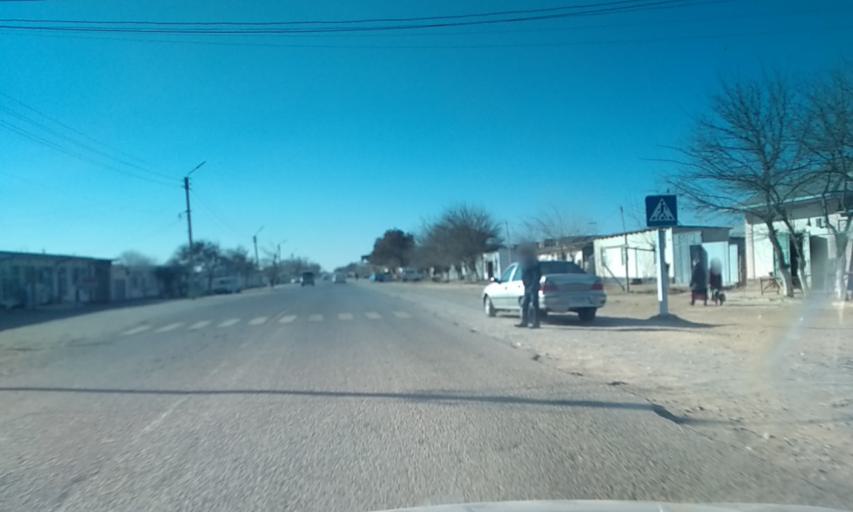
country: UZ
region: Sirdaryo
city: Guliston
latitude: 40.4938
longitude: 68.8087
